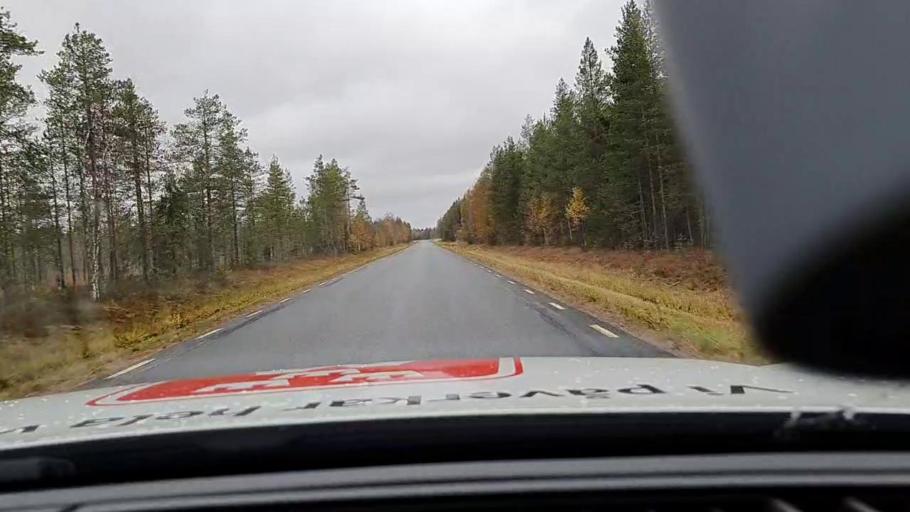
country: SE
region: Norrbotten
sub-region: Haparanda Kommun
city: Haparanda
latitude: 65.9270
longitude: 23.8189
